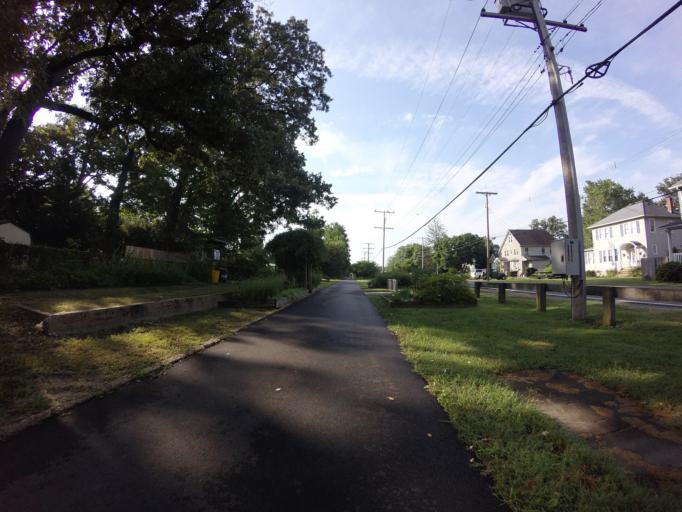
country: US
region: Maryland
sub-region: Anne Arundel County
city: Glen Burnie
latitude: 39.1554
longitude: -76.6189
